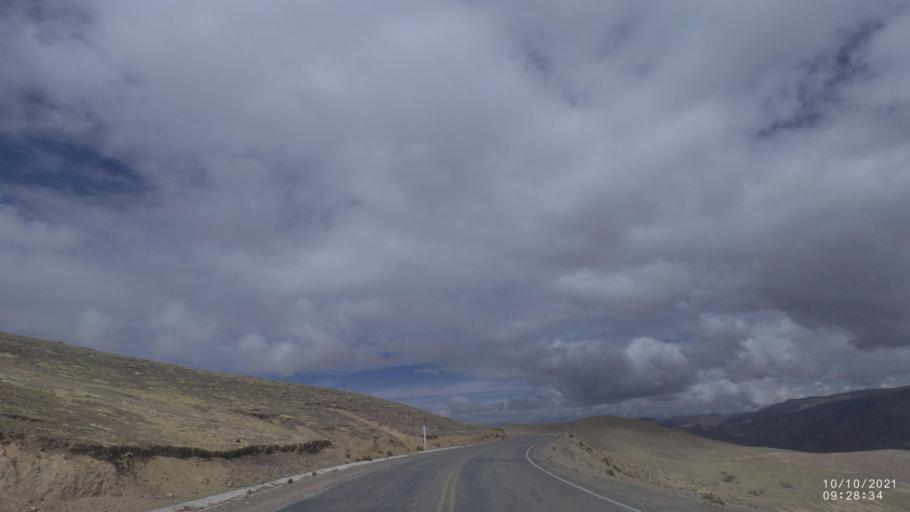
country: BO
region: La Paz
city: Quime
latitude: -17.1082
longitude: -67.3233
